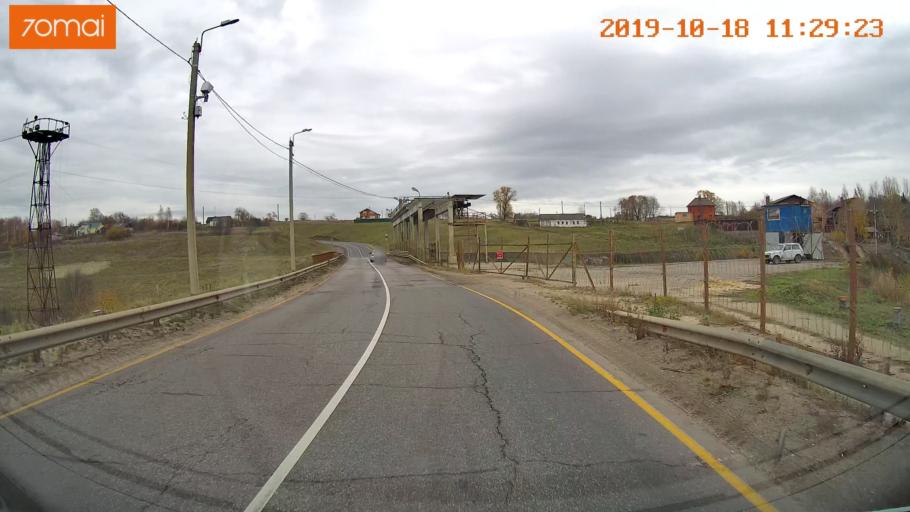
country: RU
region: Rjazan
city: Oktyabr'skiy
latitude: 54.1564
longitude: 38.6765
